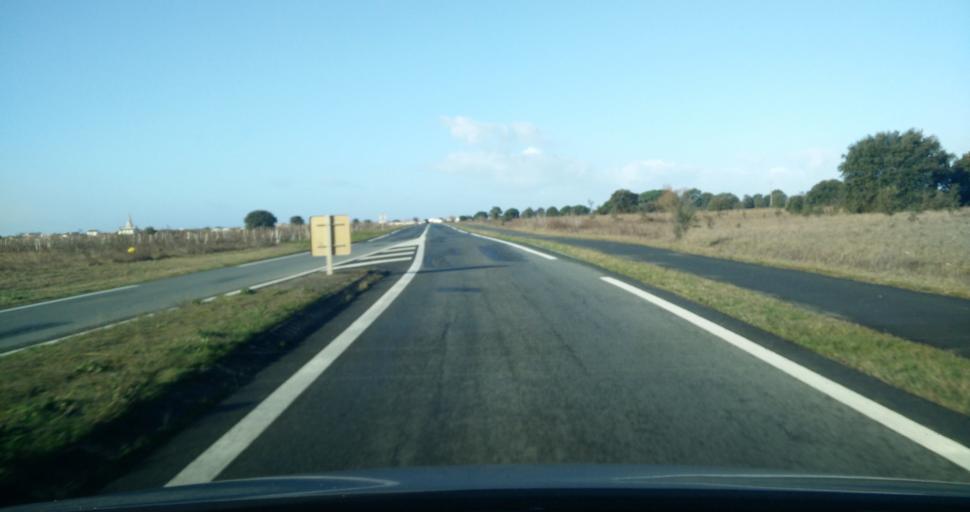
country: FR
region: Poitou-Charentes
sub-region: Departement de la Charente-Maritime
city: Sainte-Marie-de-Re
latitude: 46.1538
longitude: -1.2959
